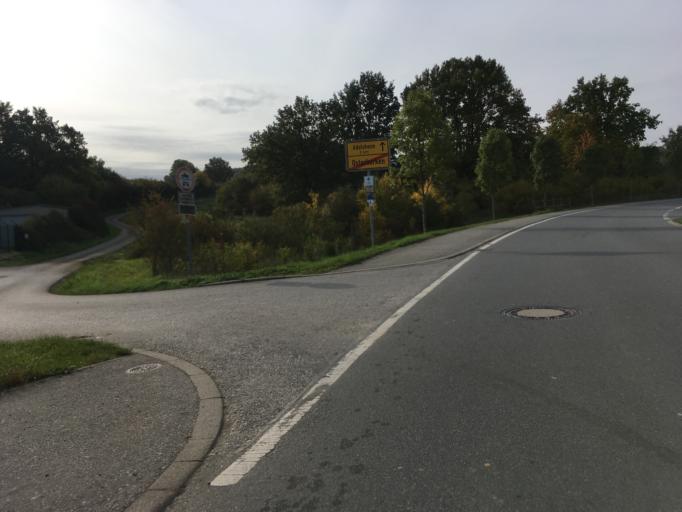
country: DE
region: Baden-Wuerttemberg
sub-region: Karlsruhe Region
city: Osterburken
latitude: 49.4199
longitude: 9.4139
